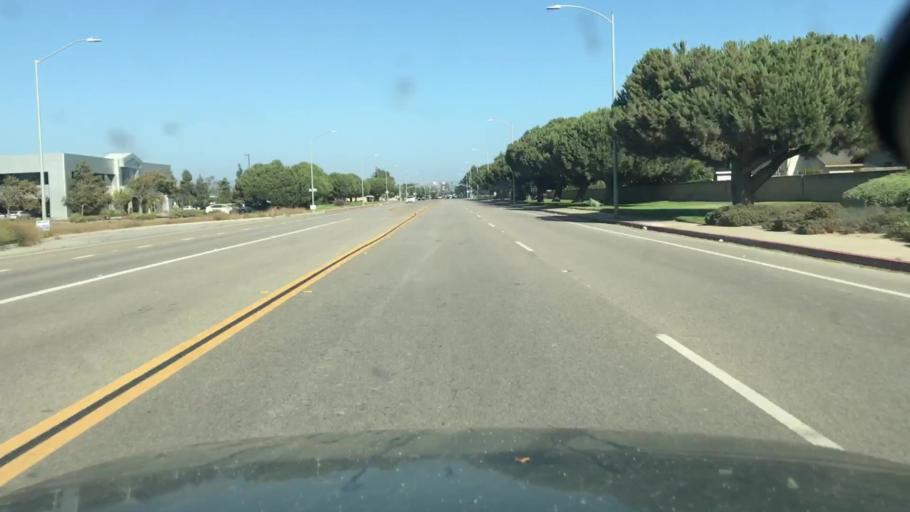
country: US
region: California
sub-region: Santa Barbara County
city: Lompoc
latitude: 34.6609
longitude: -120.4703
